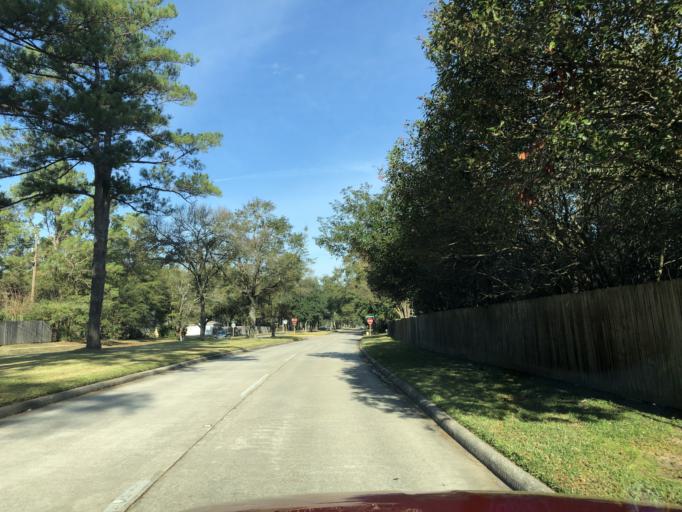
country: US
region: Texas
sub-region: Harris County
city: Tomball
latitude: 30.0186
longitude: -95.5448
